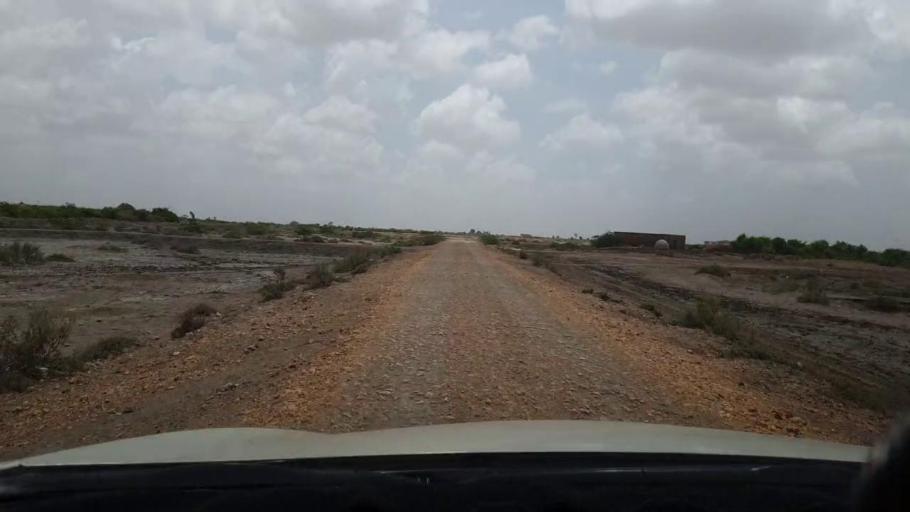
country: PK
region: Sindh
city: Kadhan
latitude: 24.3964
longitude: 68.9361
